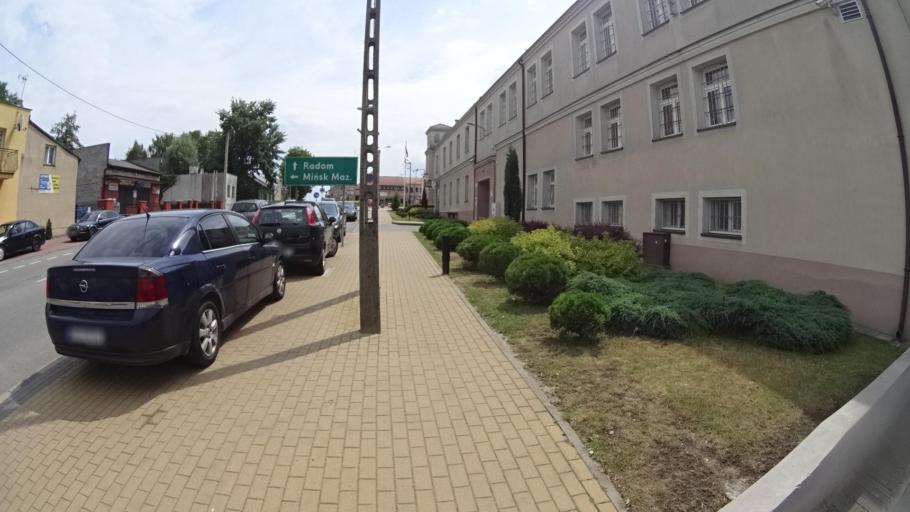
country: PL
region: Masovian Voivodeship
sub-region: Powiat grojecki
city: Grojec
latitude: 51.8693
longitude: 20.8651
